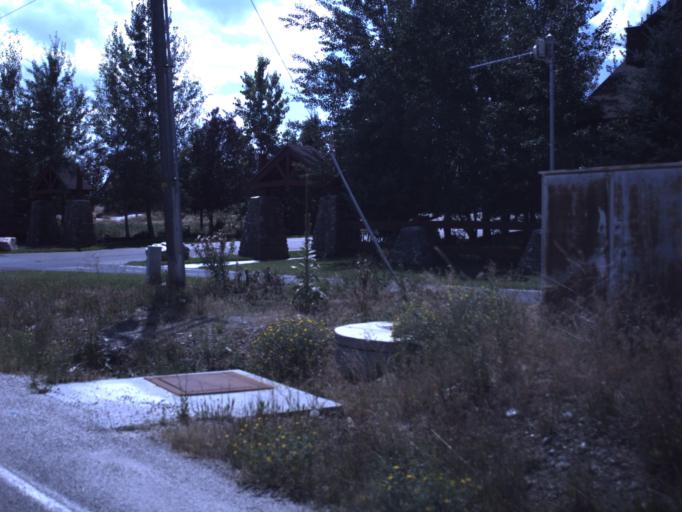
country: US
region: Idaho
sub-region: Bear Lake County
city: Paris
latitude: 41.9597
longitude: -111.4005
